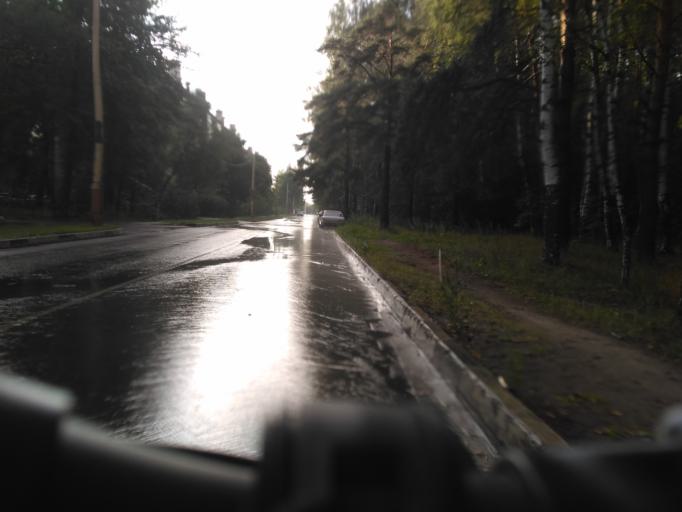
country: RU
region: Moskovskaya
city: Dubna
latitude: 56.7532
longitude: 37.2025
